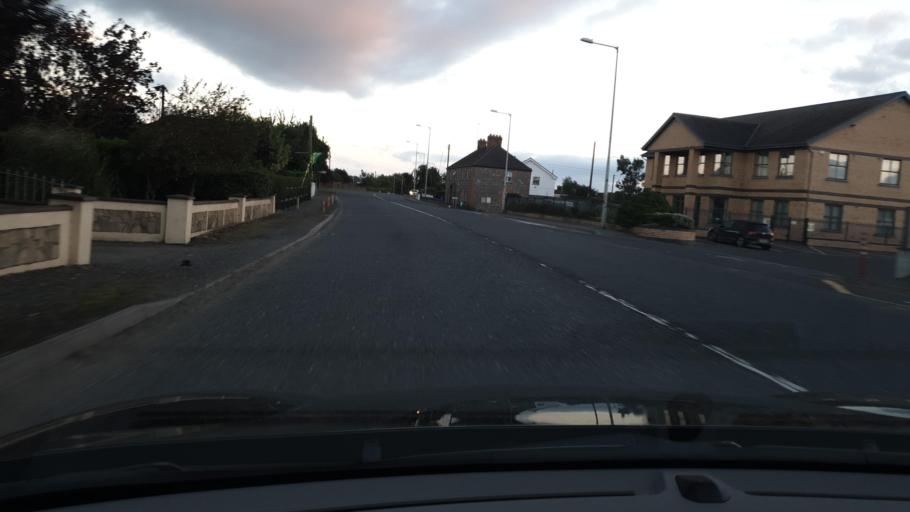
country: IE
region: Leinster
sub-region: An Mhi
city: Duleek
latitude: 53.6669
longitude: -6.3989
